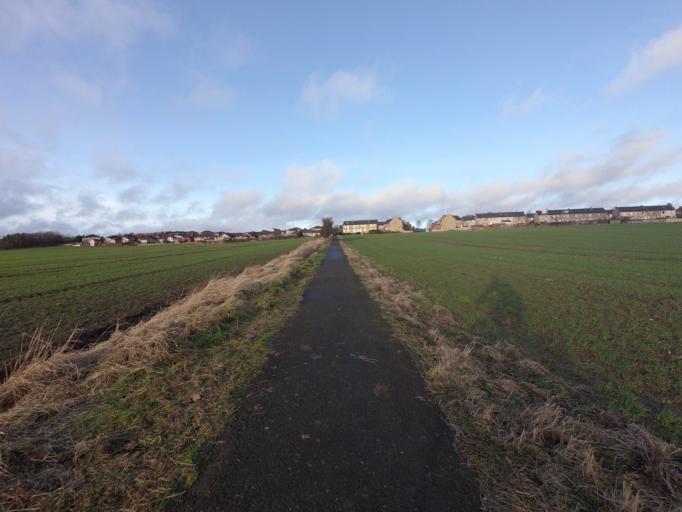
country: GB
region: Scotland
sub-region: West Lothian
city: West Calder
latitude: 55.8750
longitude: -3.5867
